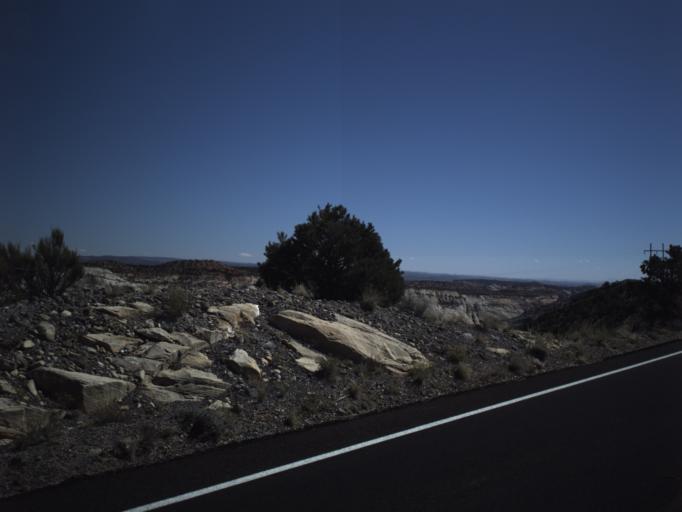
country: US
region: Utah
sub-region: Wayne County
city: Loa
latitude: 37.8316
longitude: -111.4153
